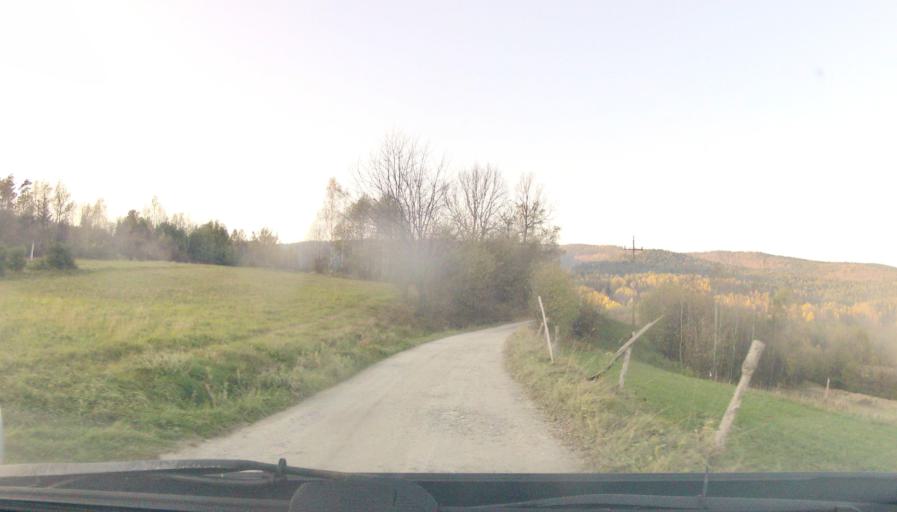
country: PL
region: Silesian Voivodeship
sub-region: Powiat zywiecki
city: Slemien
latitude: 49.7372
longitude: 19.4168
